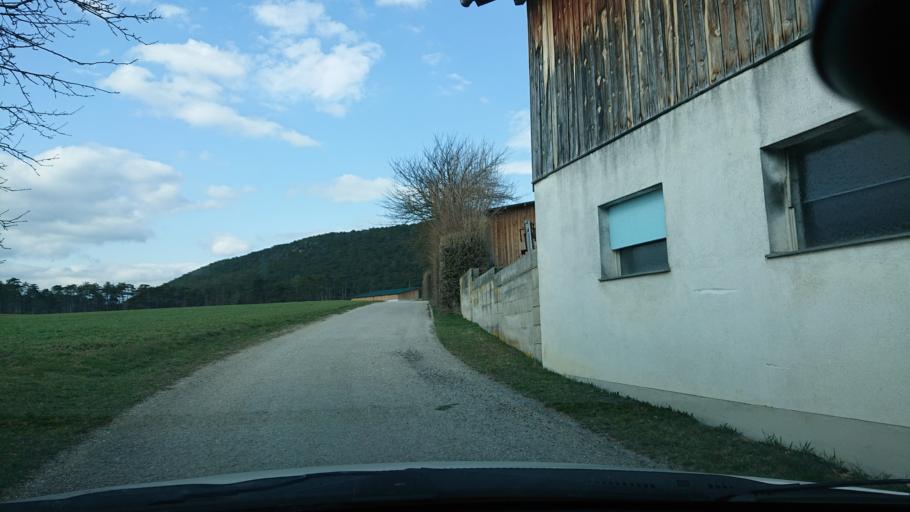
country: AT
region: Lower Austria
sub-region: Politischer Bezirk Baden
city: Berndorf
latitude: 47.9270
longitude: 16.1114
